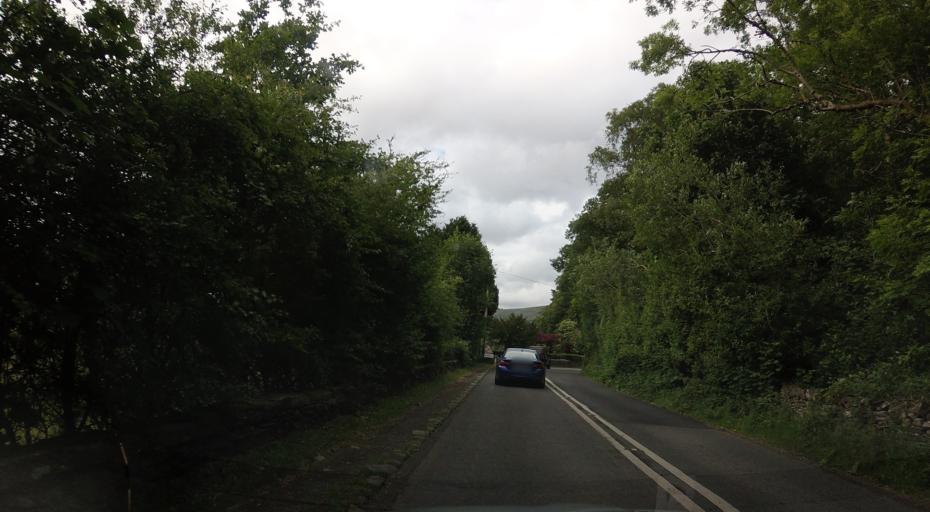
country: GB
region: England
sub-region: Cumbria
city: Keswick
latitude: 54.5493
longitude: -3.1504
